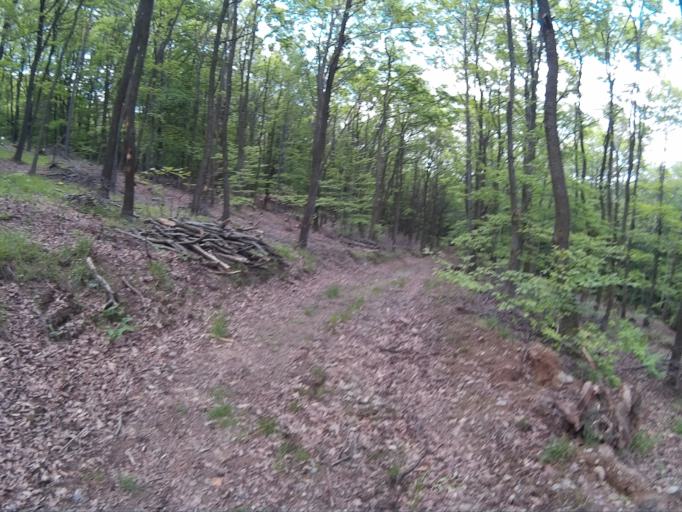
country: HU
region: Vas
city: Koszeg
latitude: 47.3737
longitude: 16.4935
